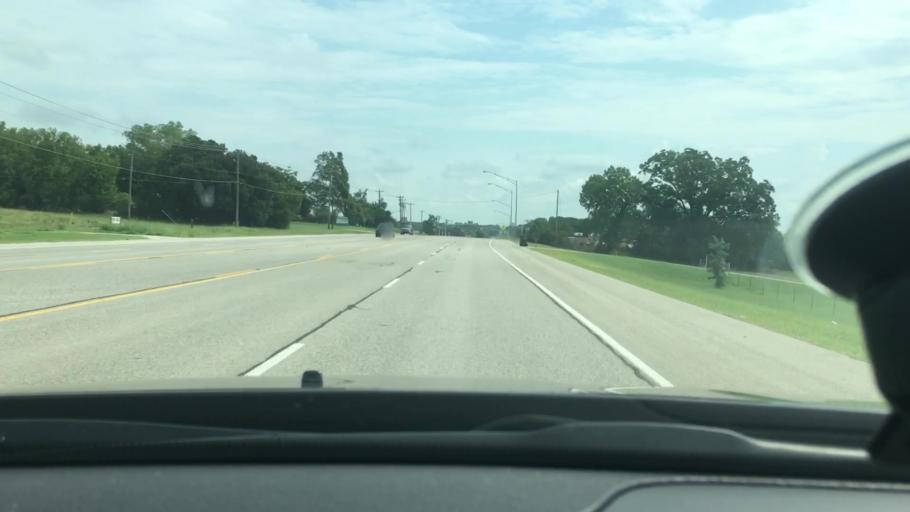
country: US
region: Oklahoma
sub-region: Carter County
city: Dickson
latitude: 34.1871
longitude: -96.9900
